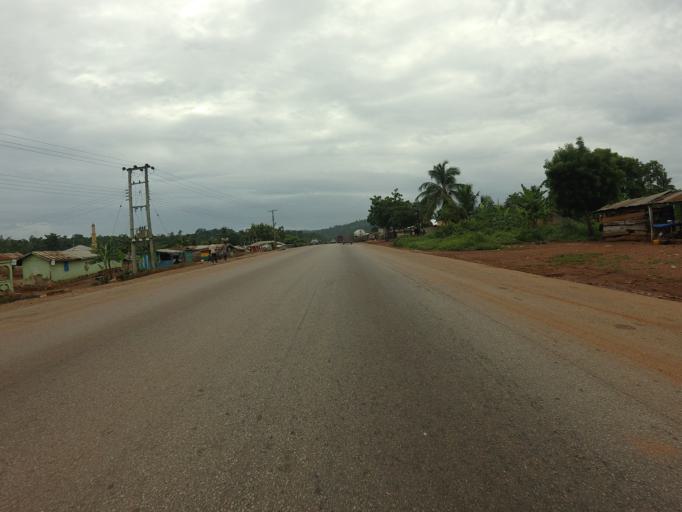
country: GH
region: Ashanti
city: Konongo
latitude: 6.6058
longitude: -1.0120
